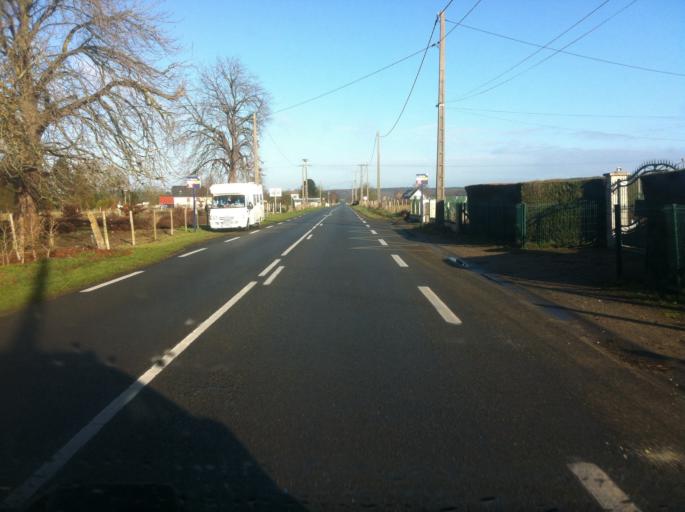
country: FR
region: Haute-Normandie
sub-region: Departement de la Seine-Maritime
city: Jumieges
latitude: 49.4408
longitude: 0.8259
